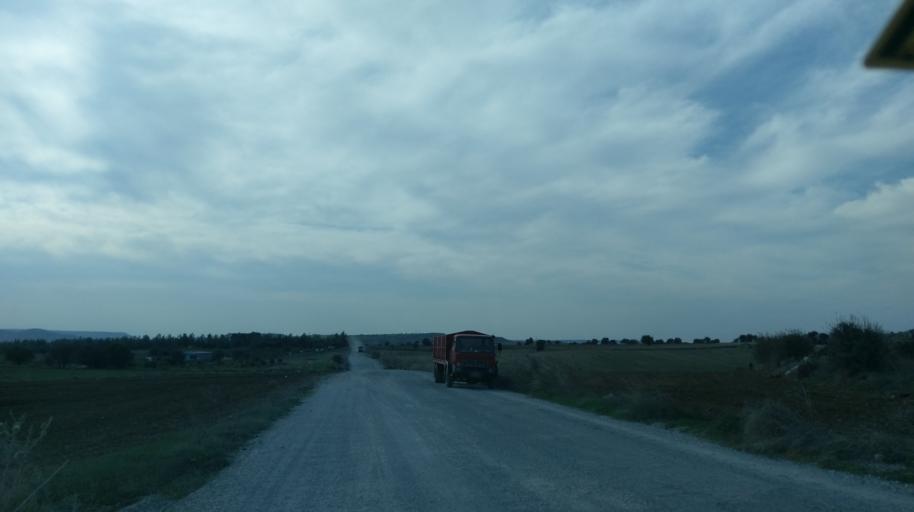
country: CY
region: Keryneia
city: Lapithos
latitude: 35.2854
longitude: 33.1739
